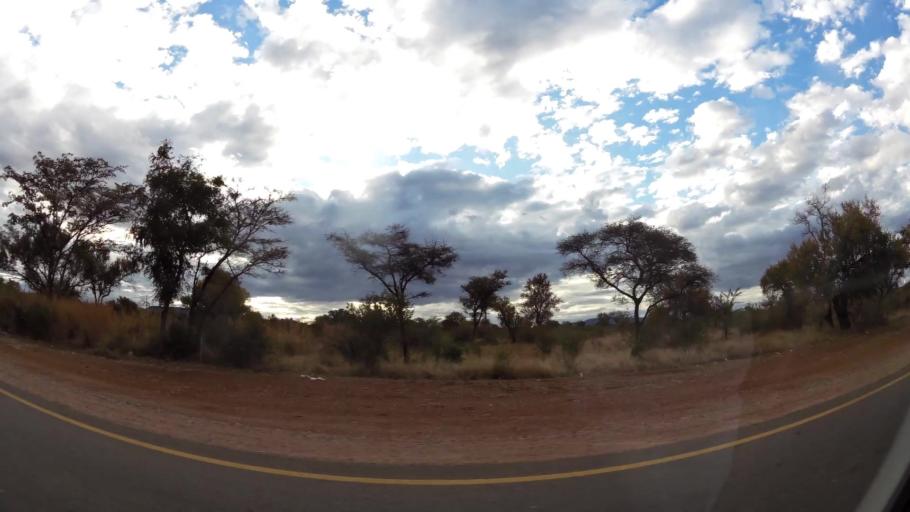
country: ZA
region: Limpopo
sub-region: Waterberg District Municipality
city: Modimolle
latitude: -24.5057
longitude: 28.7283
